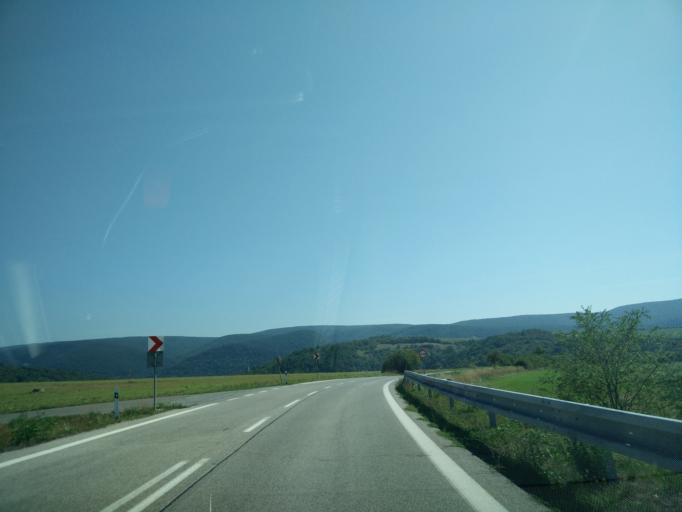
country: SK
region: Nitriansky
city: Tlmace
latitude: 48.3474
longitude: 18.5387
